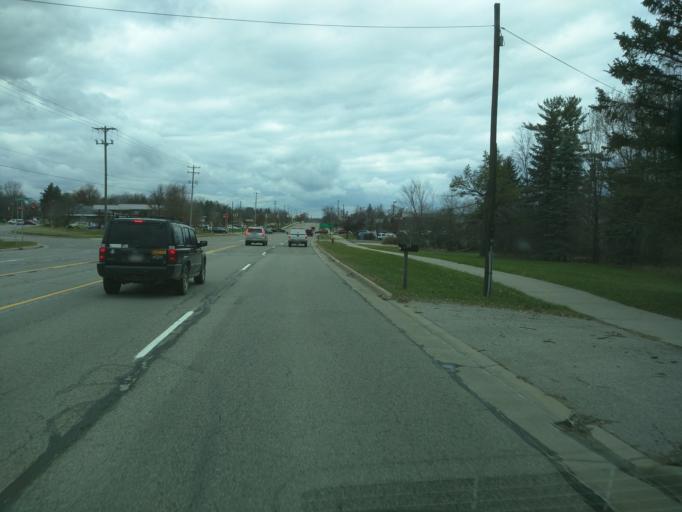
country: US
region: Michigan
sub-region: Ingham County
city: Okemos
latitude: 42.7173
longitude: -84.4075
